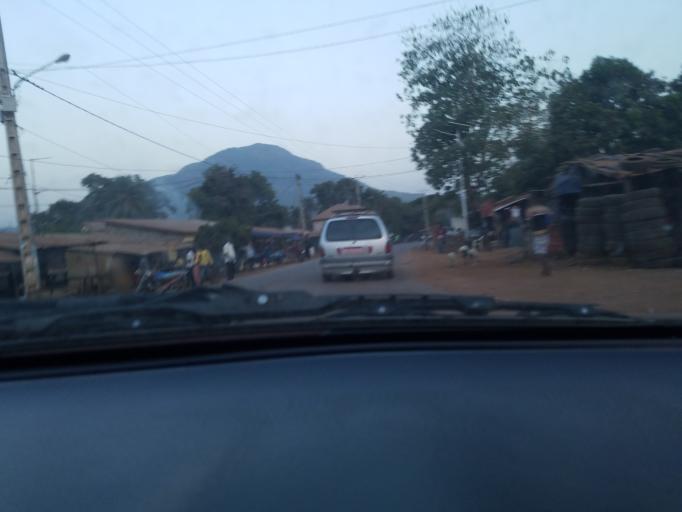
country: GN
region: Kindia
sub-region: Prefecture de Dubreka
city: Dubreka
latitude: 9.7898
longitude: -13.4896
